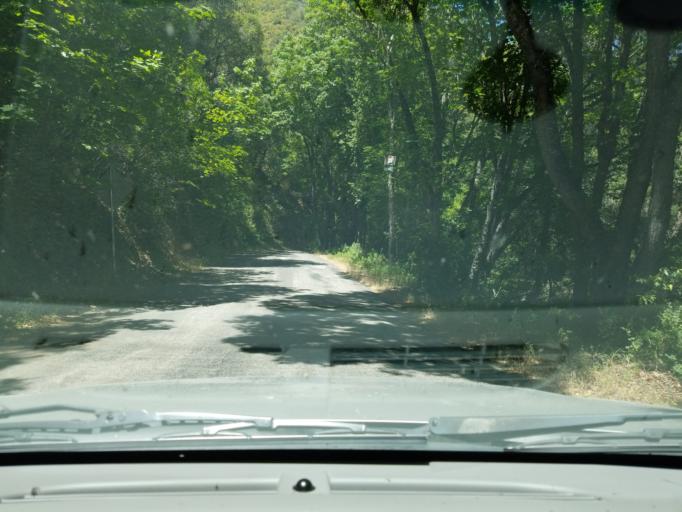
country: US
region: California
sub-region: Monterey County
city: Gonzales
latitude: 36.3646
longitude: -121.5550
